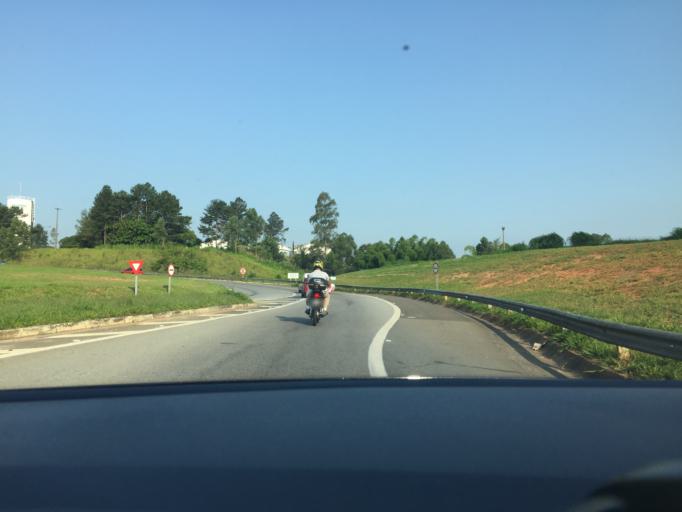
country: BR
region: Sao Paulo
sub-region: Valinhos
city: Valinhos
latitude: -23.0104
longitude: -47.0238
